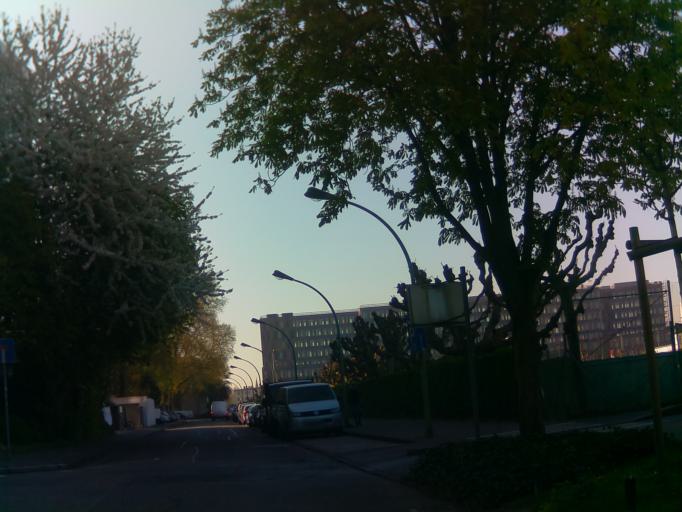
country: DE
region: Hesse
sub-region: Regierungsbezirk Darmstadt
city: Frankfurt am Main
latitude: 50.1367
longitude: 8.6805
